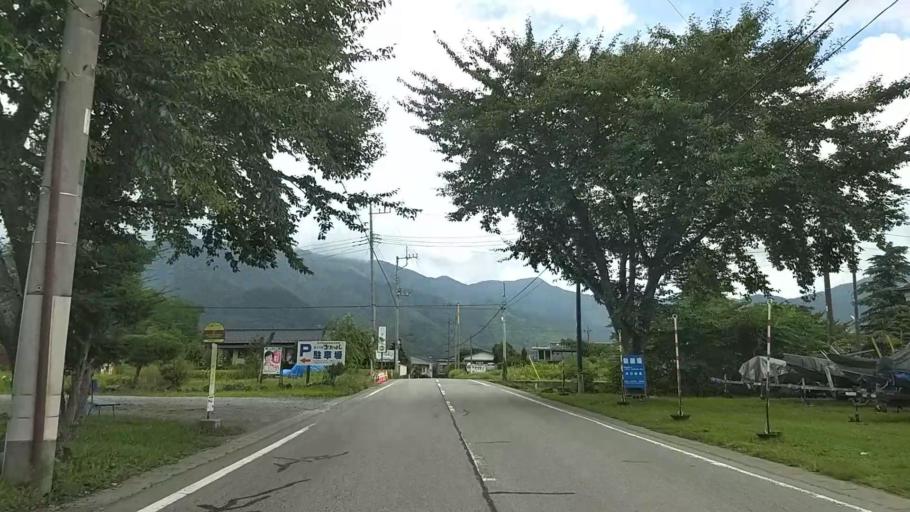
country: JP
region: Yamanashi
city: Fujikawaguchiko
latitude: 35.5090
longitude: 138.7591
